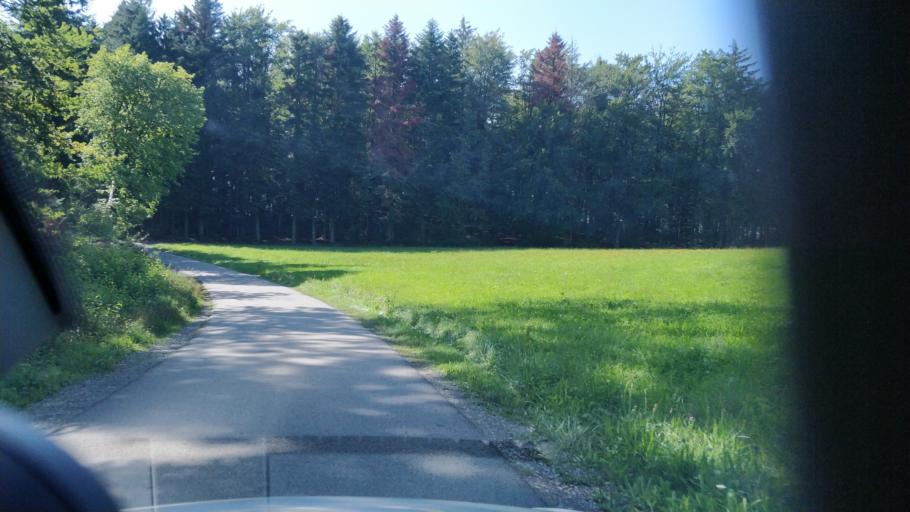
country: DE
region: Baden-Wuerttemberg
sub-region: Regierungsbezirk Stuttgart
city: Oberrot
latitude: 49.0189
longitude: 9.6145
